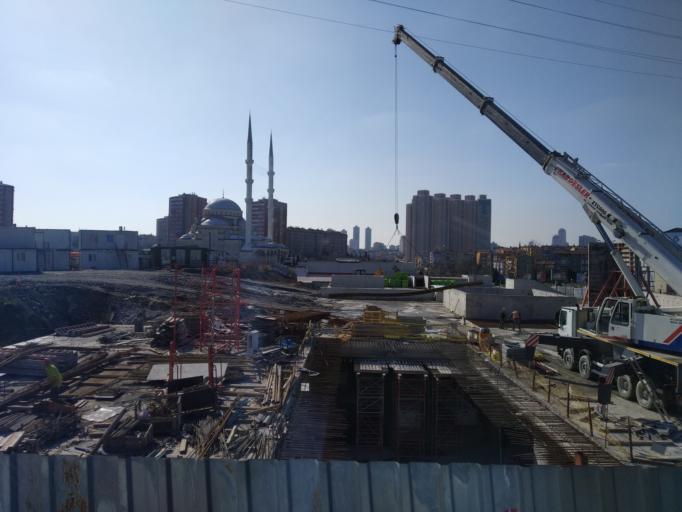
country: TR
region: Istanbul
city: Umraniye
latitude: 40.9922
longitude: 29.1540
